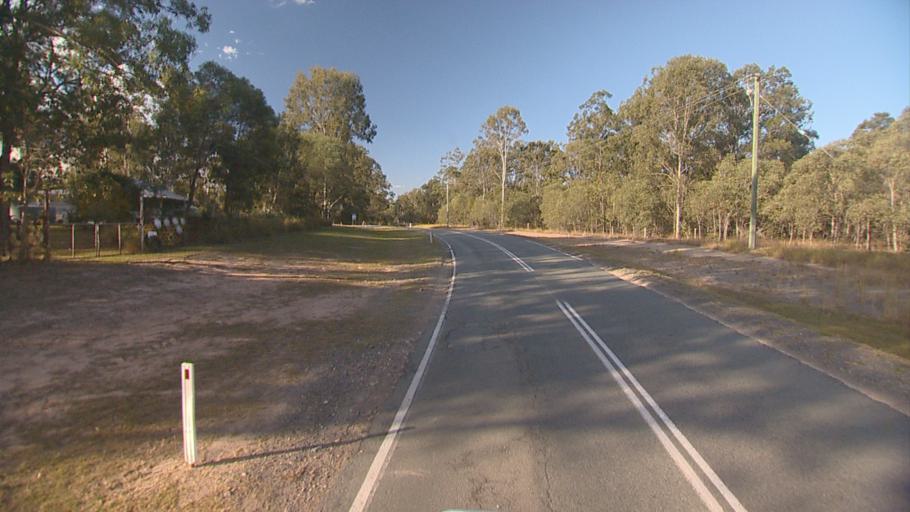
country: AU
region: Queensland
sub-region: Ipswich
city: Springfield Lakes
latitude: -27.7288
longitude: 152.9518
